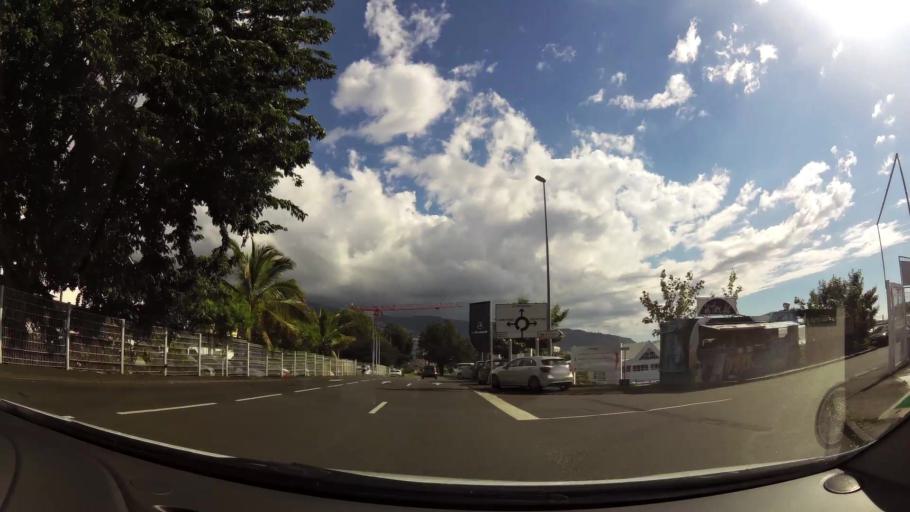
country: RE
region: Reunion
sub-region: Reunion
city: Saint-Denis
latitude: -20.8923
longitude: 55.4931
